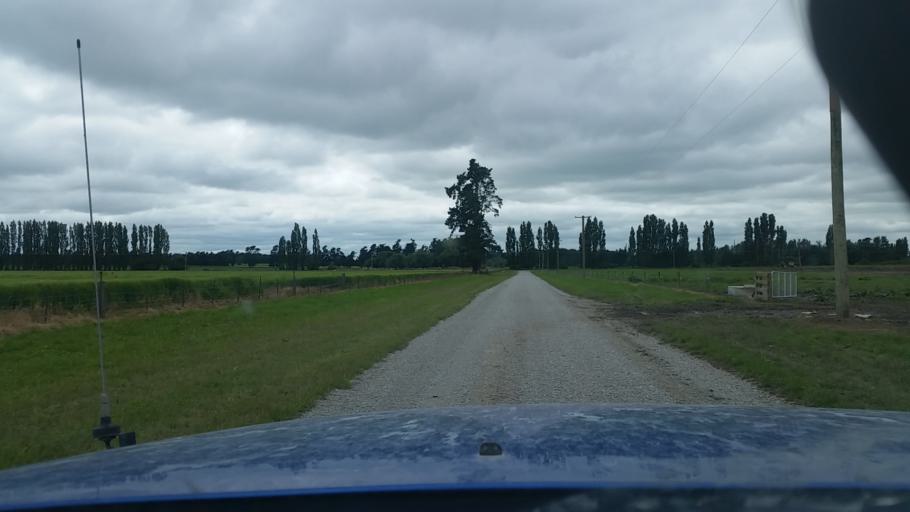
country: NZ
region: Canterbury
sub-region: Ashburton District
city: Methven
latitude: -43.8054
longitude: 171.4118
